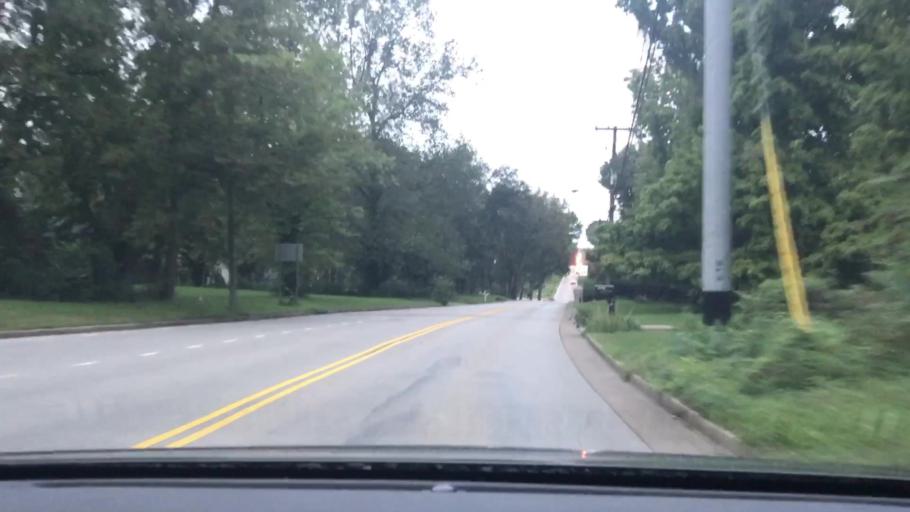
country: US
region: Tennessee
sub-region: Williamson County
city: Brentwood Estates
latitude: 36.0332
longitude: -86.7688
